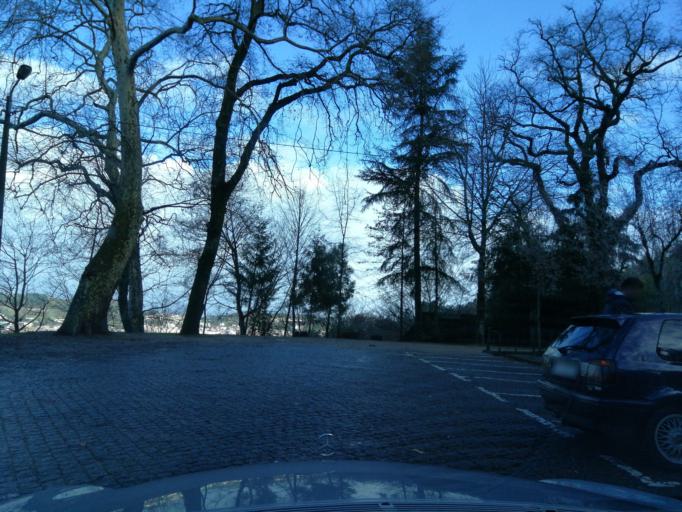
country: PT
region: Braga
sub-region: Braga
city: Adaufe
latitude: 41.5545
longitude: -8.3810
